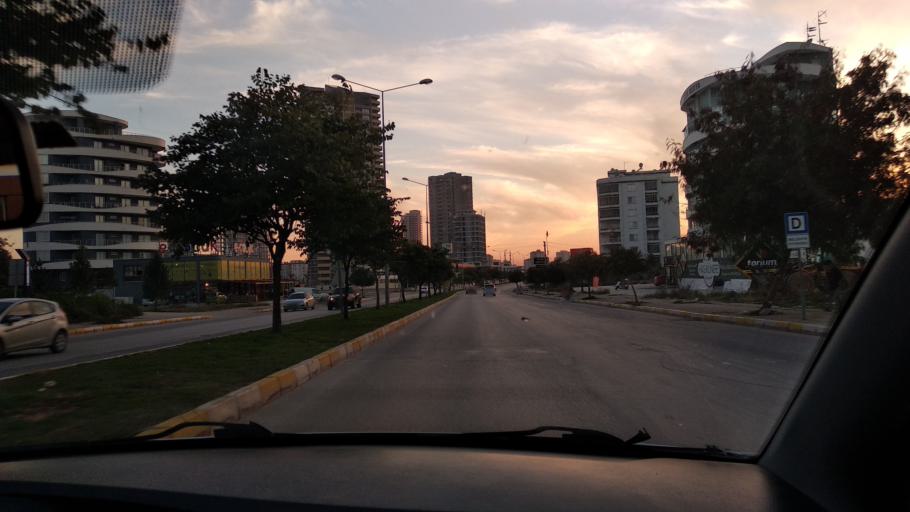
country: TR
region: Mersin
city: Mercin
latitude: 36.8023
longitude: 34.5839
